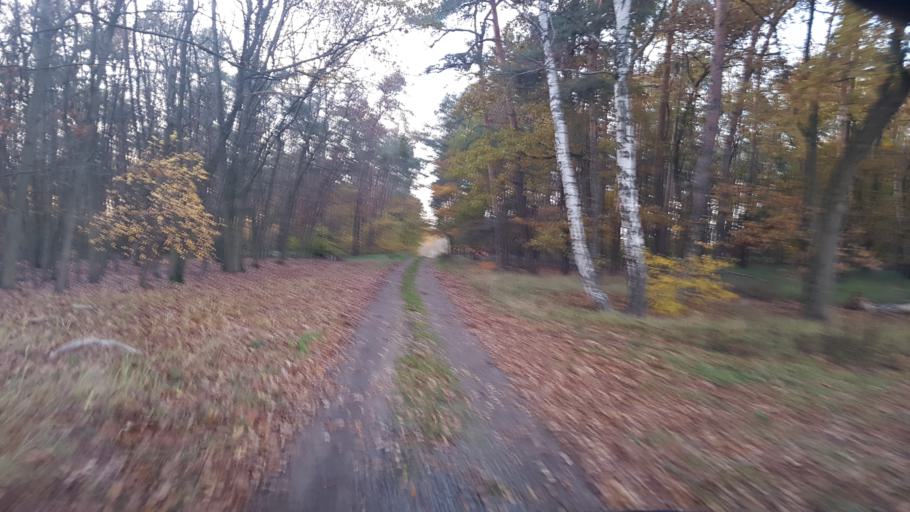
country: DE
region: Brandenburg
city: Schilda
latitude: 51.5910
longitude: 13.3184
